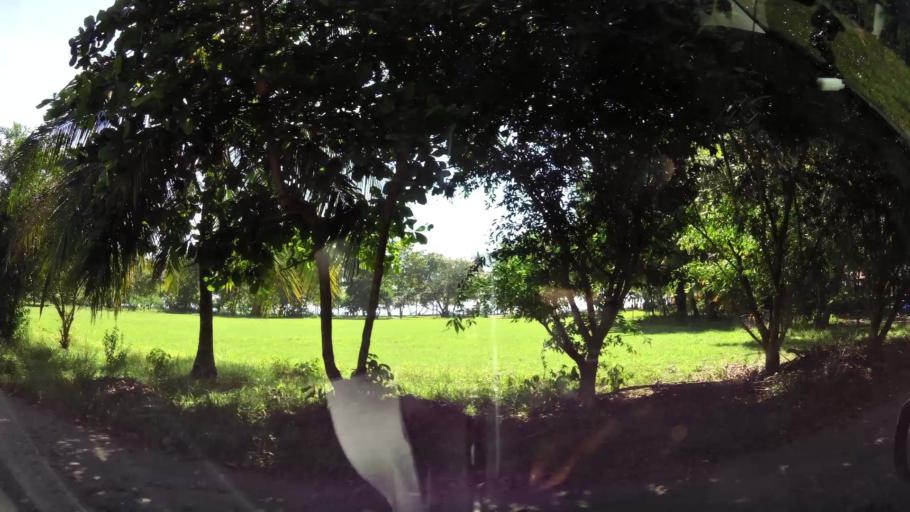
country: CR
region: Puntarenas
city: Quepos
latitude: 9.3204
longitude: -83.9605
